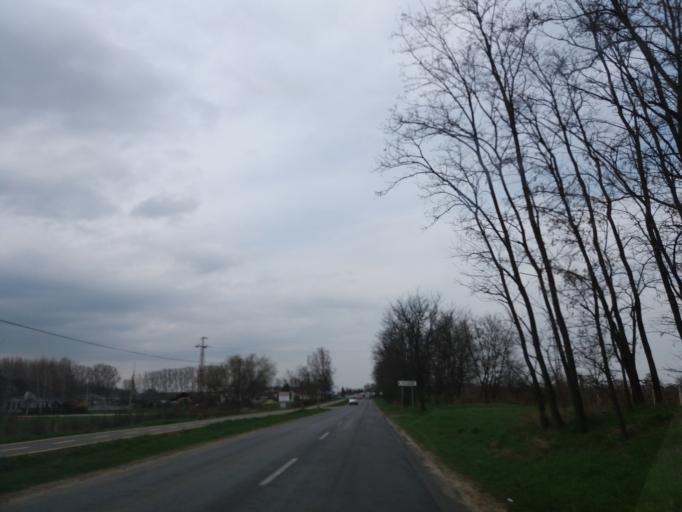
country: HU
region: Szabolcs-Szatmar-Bereg
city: Anarcs
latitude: 48.1956
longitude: 22.0967
